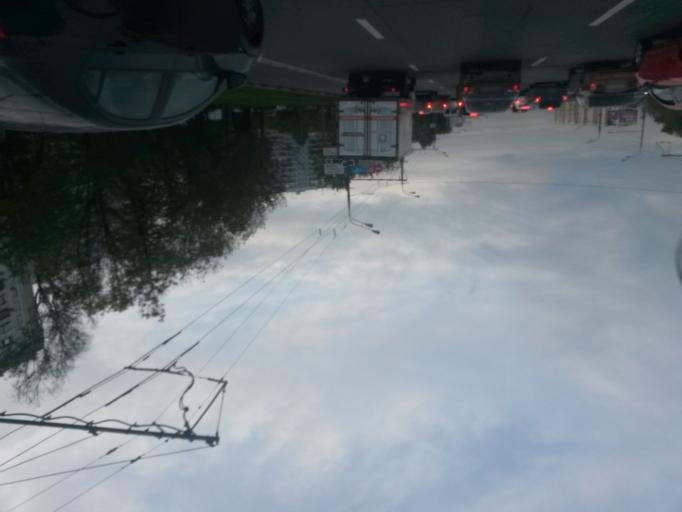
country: RU
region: Moscow
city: Chertanovo Yuzhnoye
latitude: 55.5913
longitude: 37.5999
